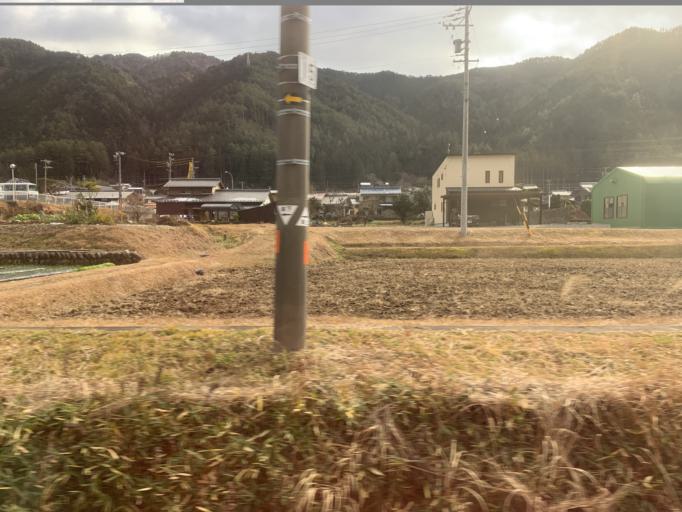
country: JP
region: Gifu
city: Takayama
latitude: 35.9302
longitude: 137.2428
